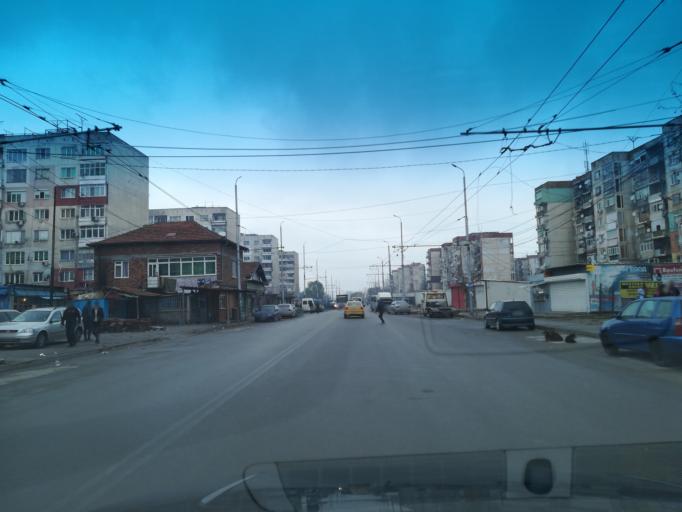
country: BG
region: Plovdiv
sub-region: Obshtina Plovdiv
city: Plovdiv
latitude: 42.1596
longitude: 24.7858
